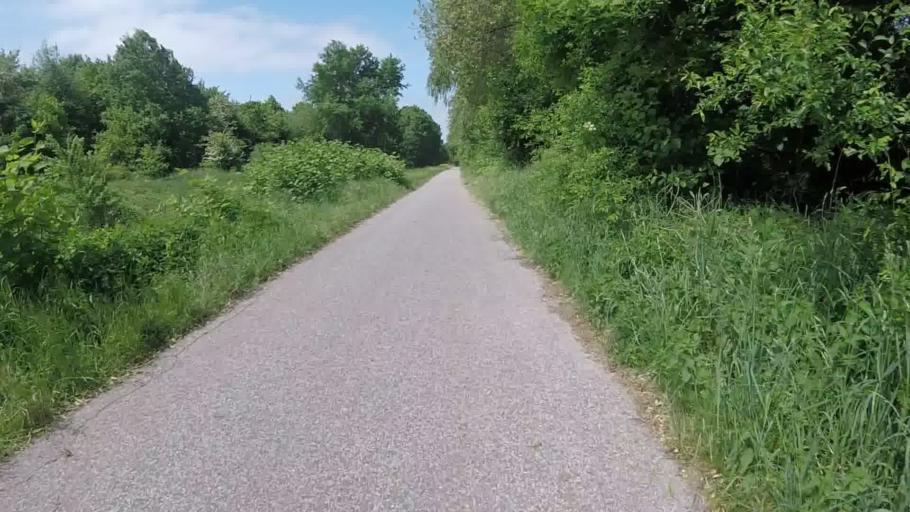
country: DE
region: Schleswig-Holstein
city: Oststeinbek
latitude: 53.4942
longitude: 10.1422
